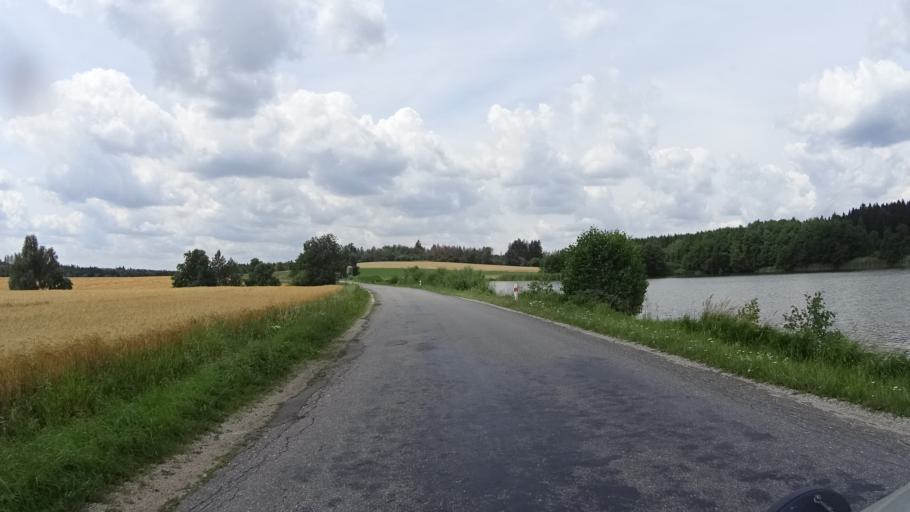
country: CZ
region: Vysocina
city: Merin
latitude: 49.4114
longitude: 15.9395
